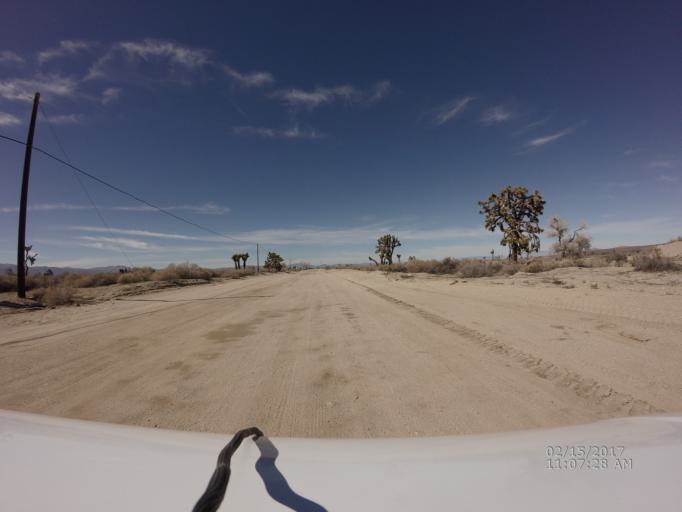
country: US
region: California
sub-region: Los Angeles County
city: Lake Los Angeles
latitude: 34.5874
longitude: -117.8737
